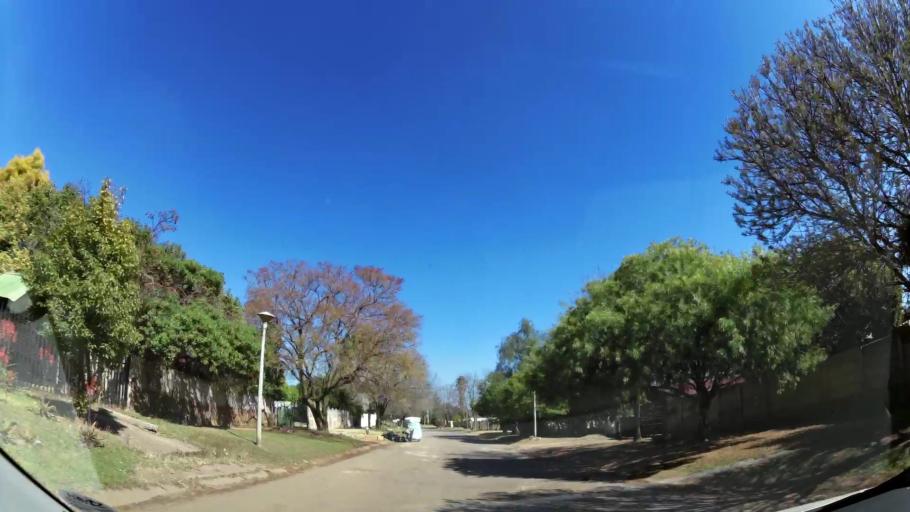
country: ZA
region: Mpumalanga
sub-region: Nkangala District Municipality
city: Witbank
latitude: -25.8485
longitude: 29.2469
